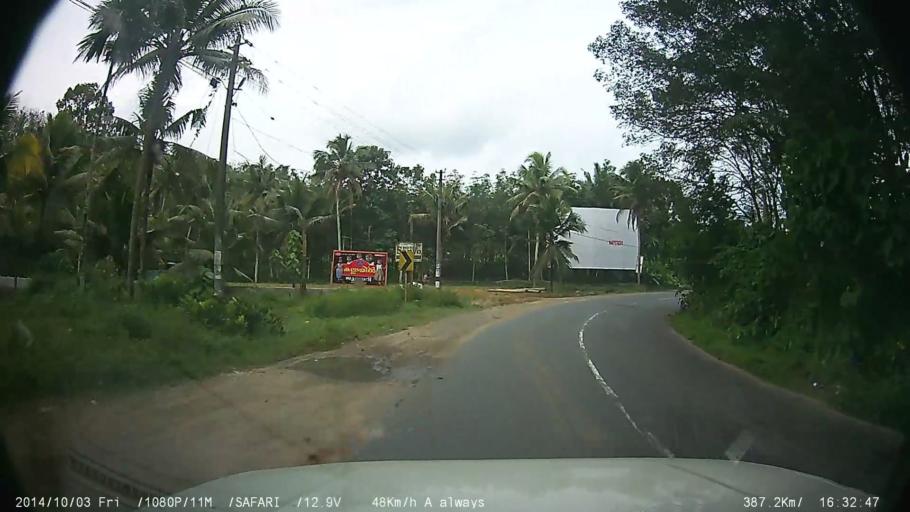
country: IN
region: Kerala
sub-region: Kottayam
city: Palackattumala
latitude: 9.8284
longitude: 76.5912
